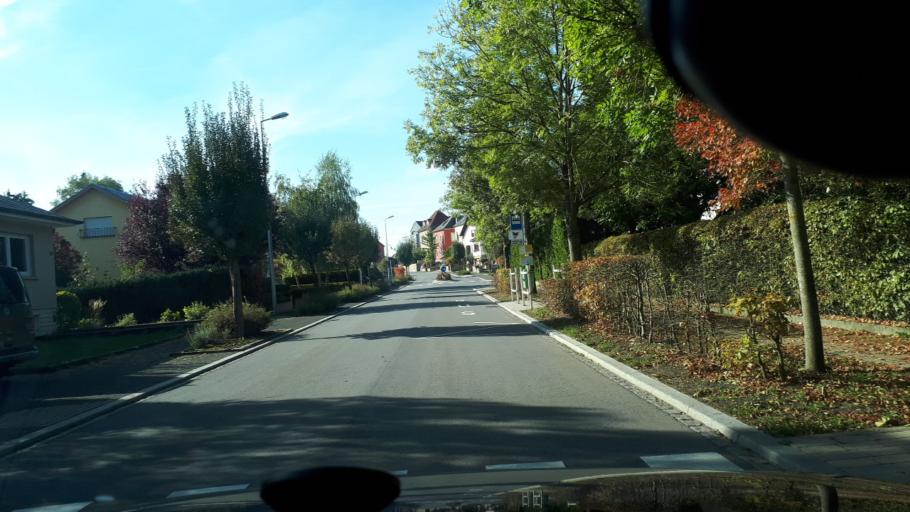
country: LU
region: Grevenmacher
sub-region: Canton de Grevenmacher
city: Flaxweiler
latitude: 49.6705
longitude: 6.3030
